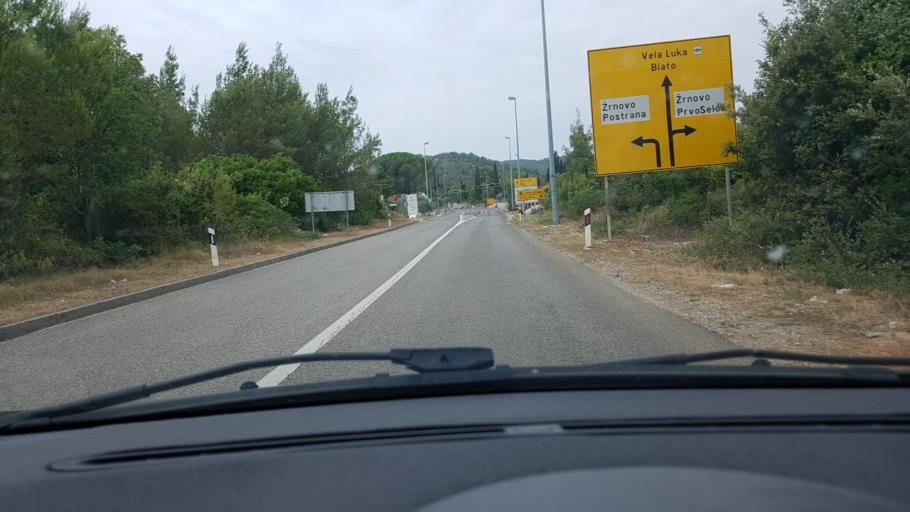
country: HR
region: Dubrovacko-Neretvanska
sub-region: Grad Korcula
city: Zrnovo
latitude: 42.9451
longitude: 17.1122
